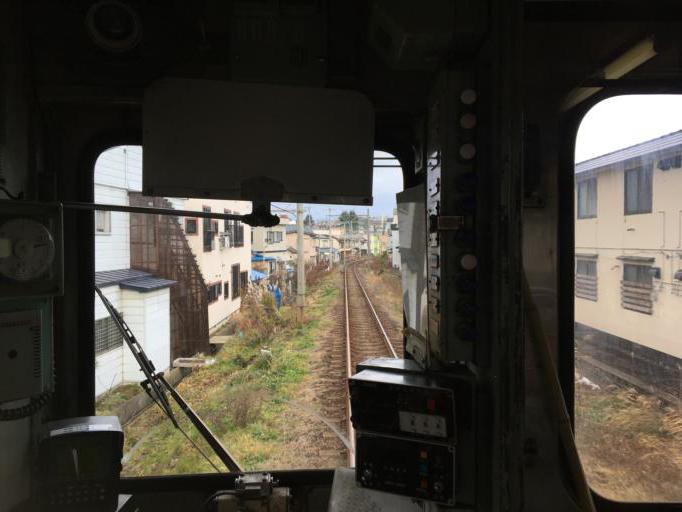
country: JP
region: Aomori
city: Hirosaki
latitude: 40.5905
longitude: 140.4685
